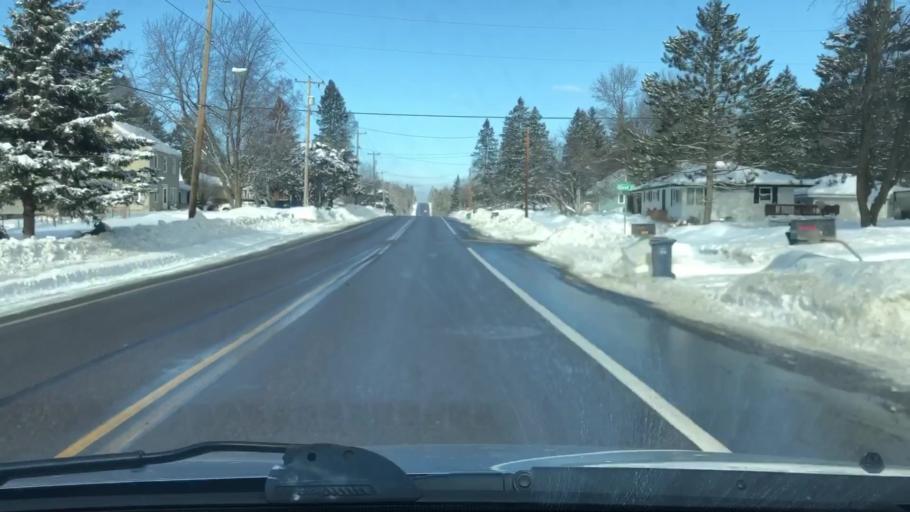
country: US
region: Minnesota
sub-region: Saint Louis County
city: Duluth
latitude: 46.8046
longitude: -92.1321
